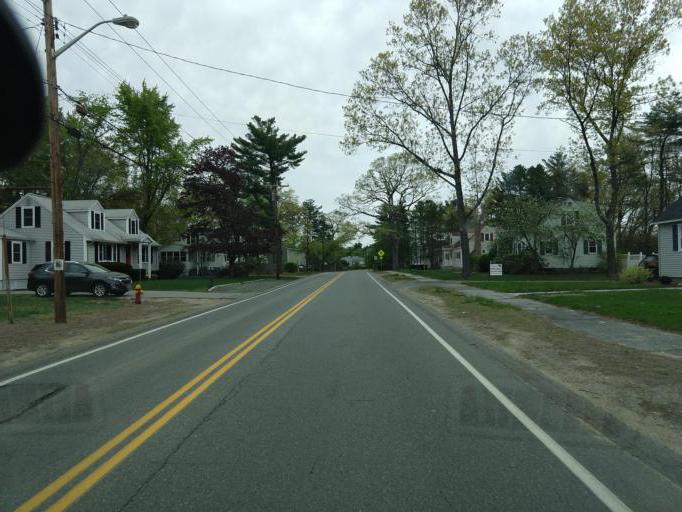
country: US
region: Massachusetts
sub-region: Middlesex County
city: Tewksbury
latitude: 42.5821
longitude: -71.2229
